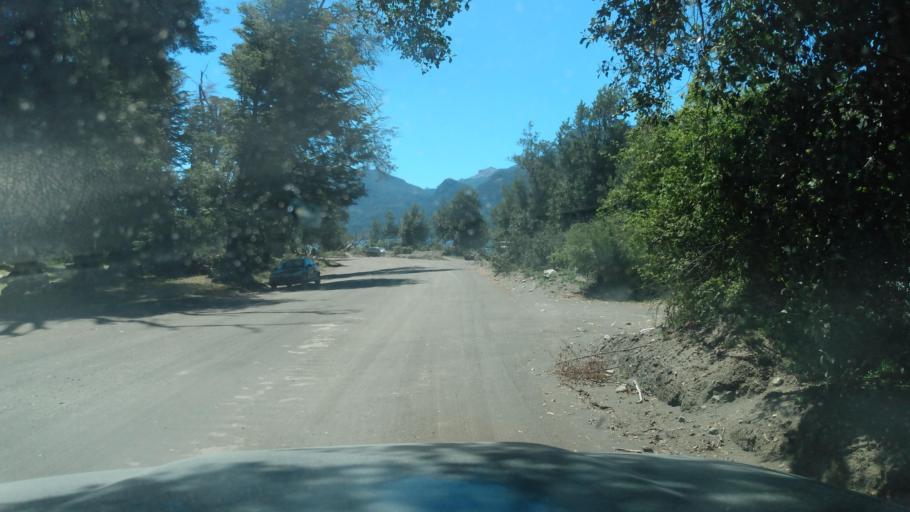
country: AR
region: Neuquen
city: Villa La Angostura
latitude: -40.6460
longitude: -71.4388
